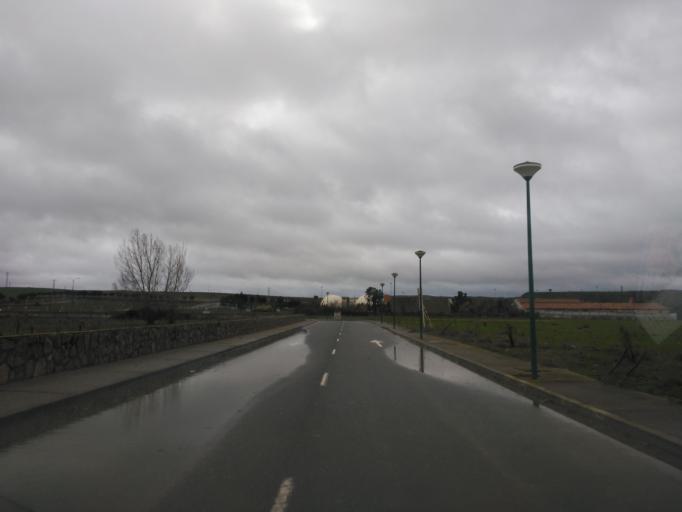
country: ES
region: Castille and Leon
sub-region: Provincia de Salamanca
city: Villamayor
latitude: 40.9770
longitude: -5.7140
